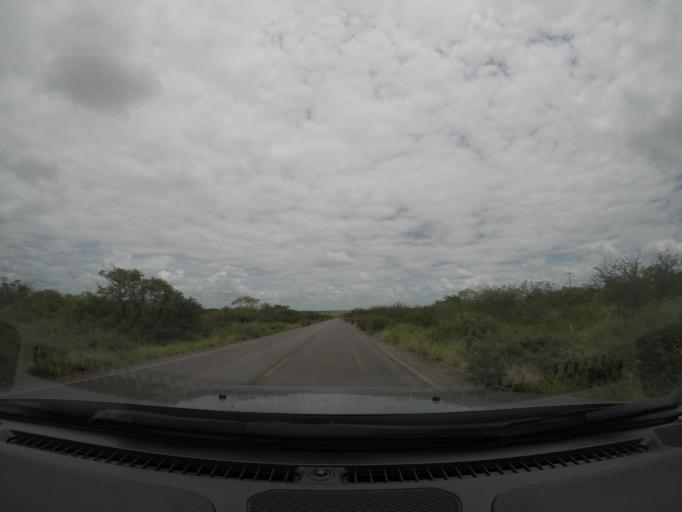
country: BR
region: Bahia
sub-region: Itaberaba
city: Itaberaba
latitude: -12.4922
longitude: -40.2350
